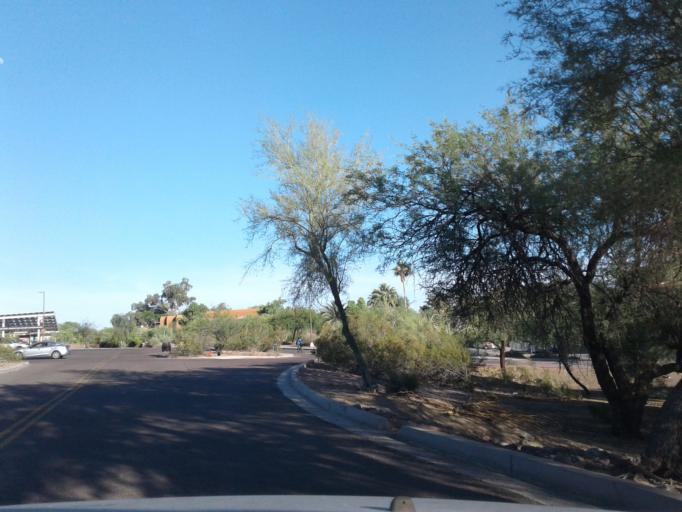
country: US
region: Arizona
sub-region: Maricopa County
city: Tempe Junction
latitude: 33.4522
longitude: -111.9505
